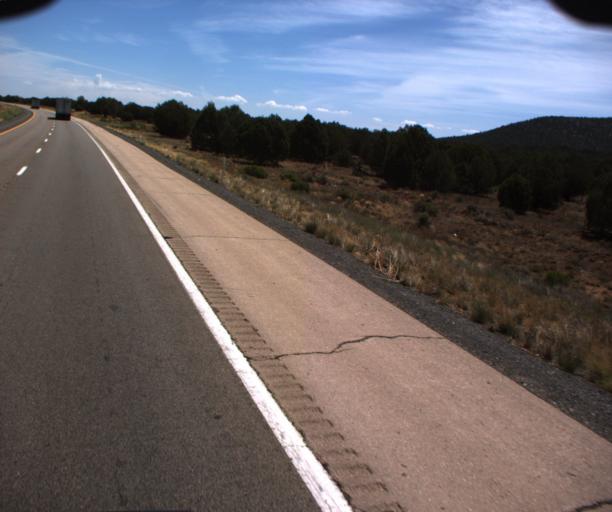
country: US
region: Arizona
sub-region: Mohave County
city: Peach Springs
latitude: 35.2079
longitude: -113.2715
